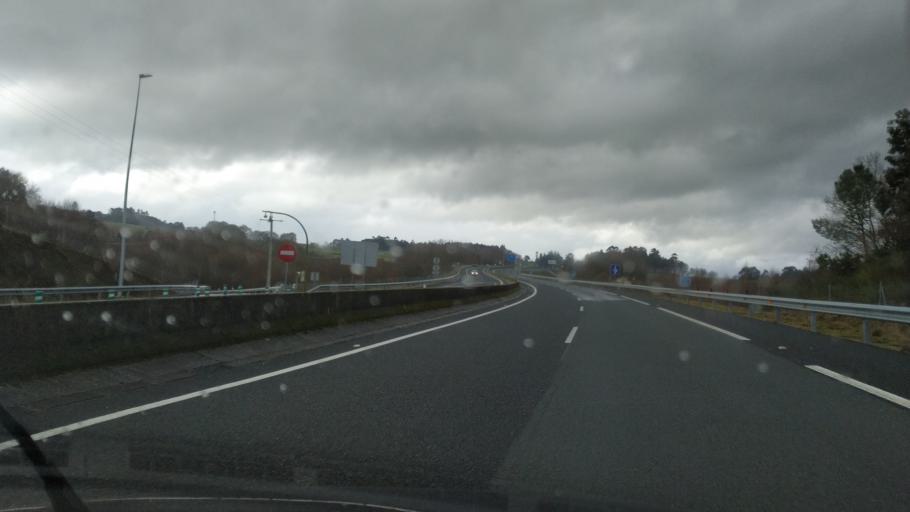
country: ES
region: Galicia
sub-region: Provincia de Pontevedra
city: Silleda
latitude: 42.7096
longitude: -8.2311
